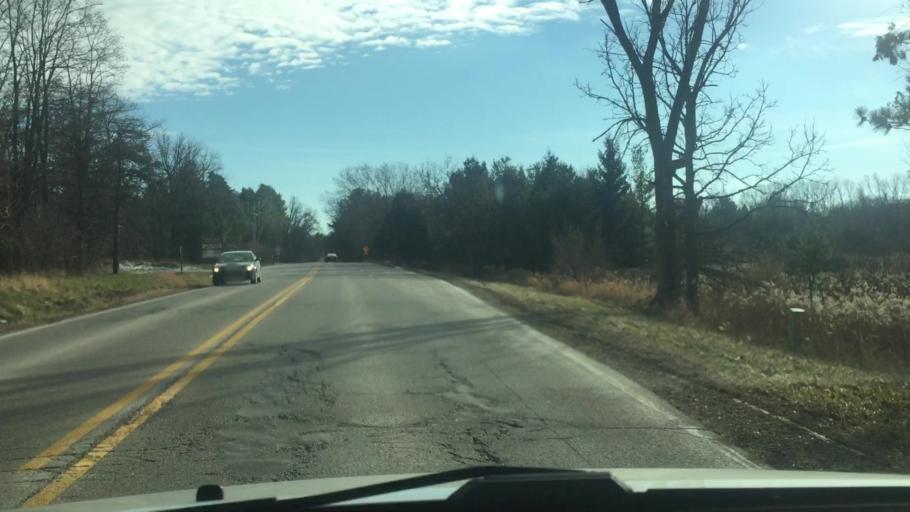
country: US
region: Wisconsin
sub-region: Waukesha County
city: Delafield
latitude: 43.0418
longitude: -88.4044
